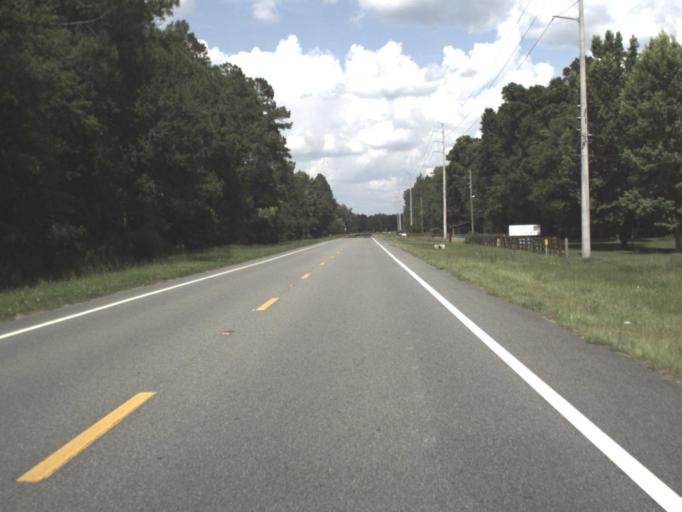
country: US
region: Florida
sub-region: Bradford County
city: Starke
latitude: 29.9519
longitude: -82.0829
